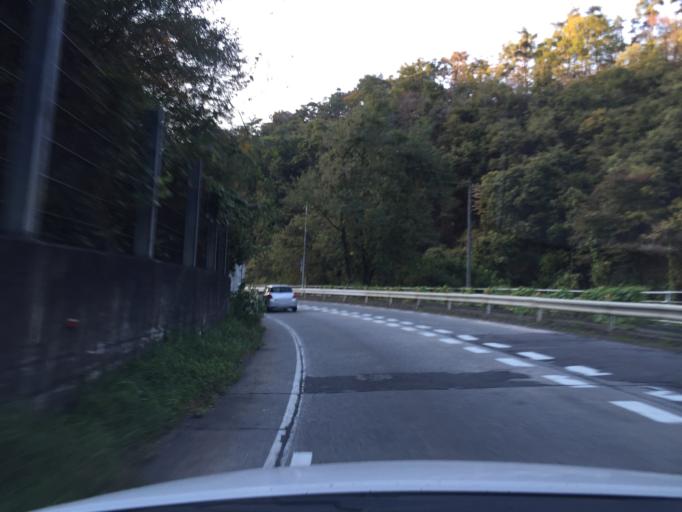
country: JP
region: Fukushima
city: Sukagawa
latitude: 37.2965
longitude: 140.5181
